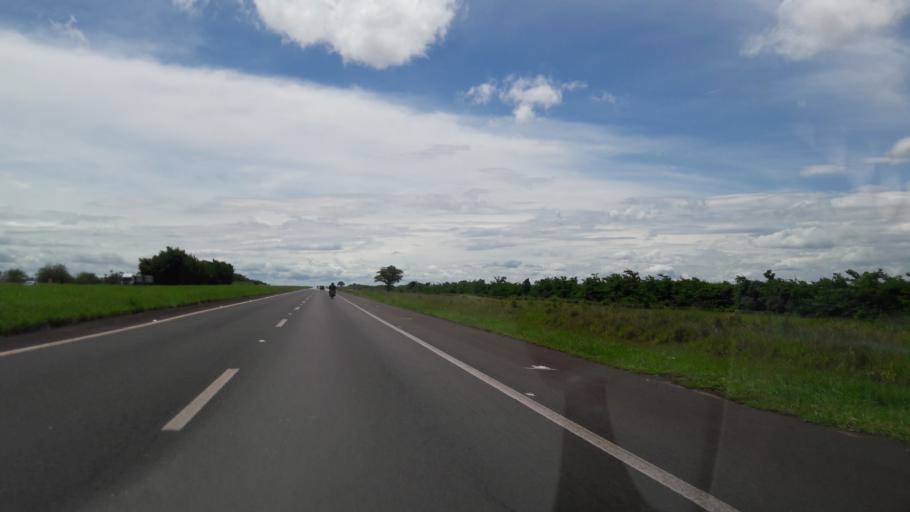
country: BR
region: Sao Paulo
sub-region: Avare
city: Avare
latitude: -22.9484
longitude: -48.8863
